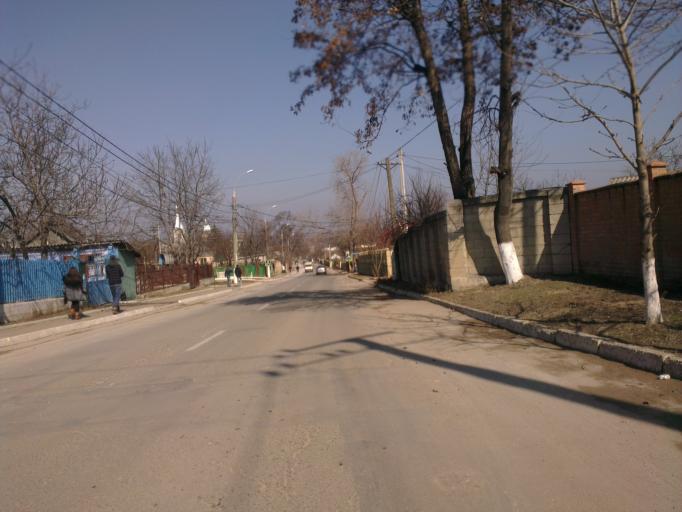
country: MD
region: Chisinau
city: Cricova
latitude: 47.1332
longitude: 28.8662
